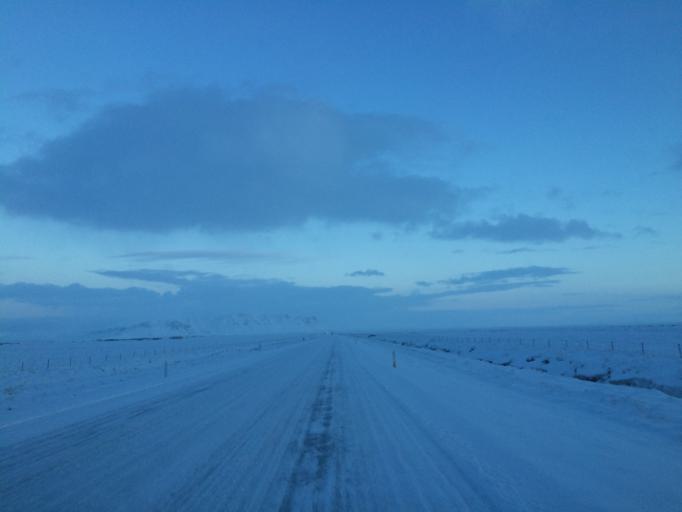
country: IS
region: South
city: Selfoss
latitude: 63.8734
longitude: -21.0955
